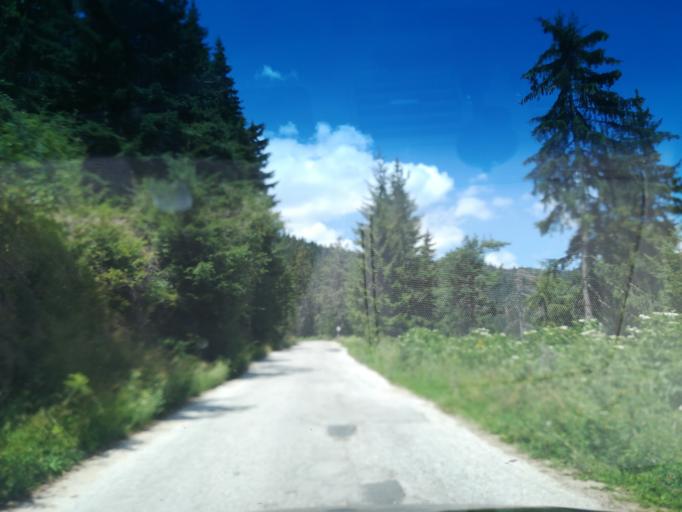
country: BG
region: Smolyan
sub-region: Obshtina Chepelare
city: Chepelare
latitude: 41.6807
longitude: 24.7714
